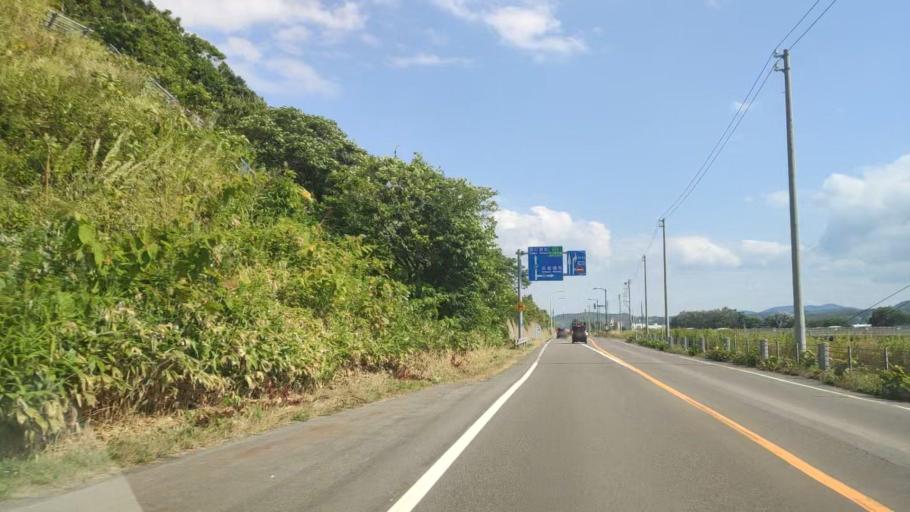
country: JP
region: Hokkaido
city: Rumoi
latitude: 43.9486
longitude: 141.6496
